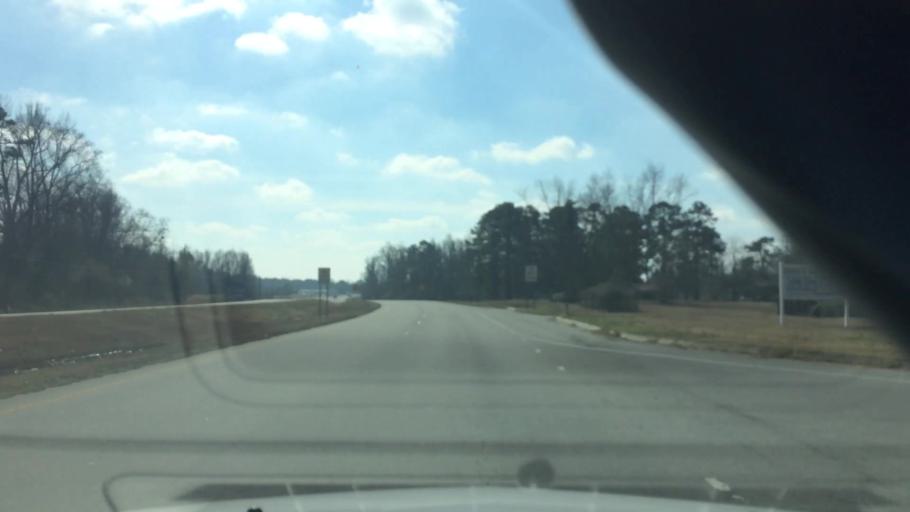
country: US
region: North Carolina
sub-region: Duplin County
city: Beulaville
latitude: 35.0855
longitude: -77.7309
